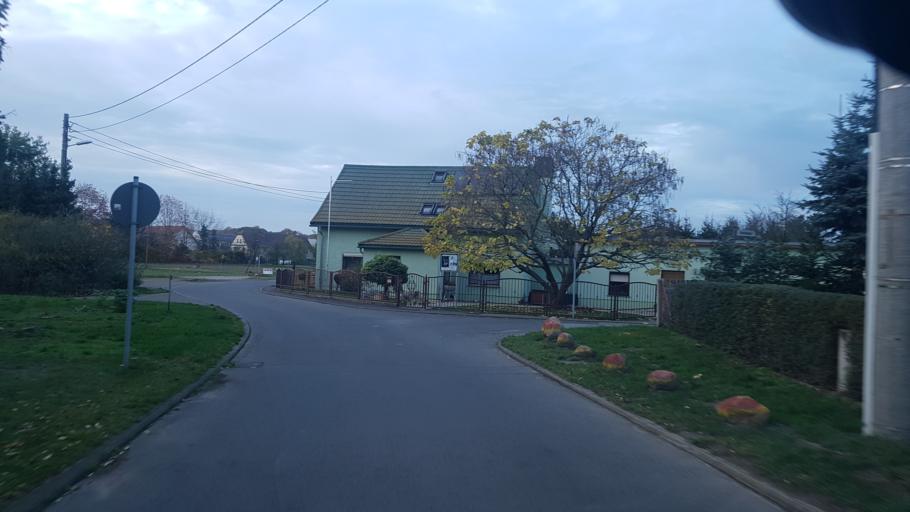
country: DE
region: Saxony
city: Dahlen
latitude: 51.3801
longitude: 13.0391
